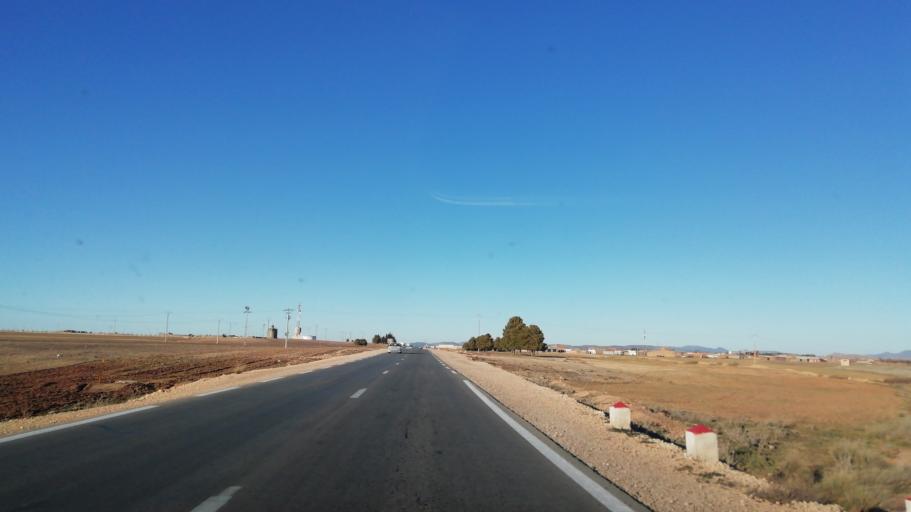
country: DZ
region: Tlemcen
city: Sebdou
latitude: 34.4731
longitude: -1.2717
